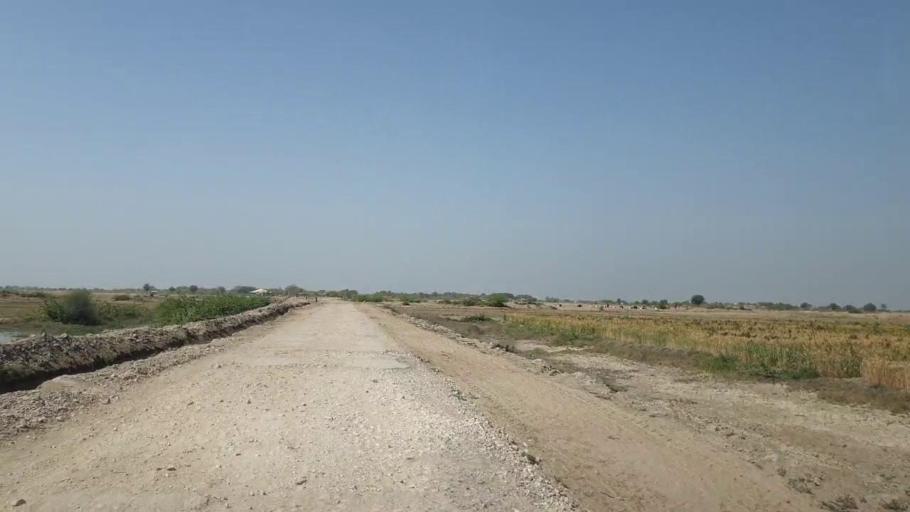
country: PK
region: Sindh
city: Naukot
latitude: 24.9747
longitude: 69.4709
